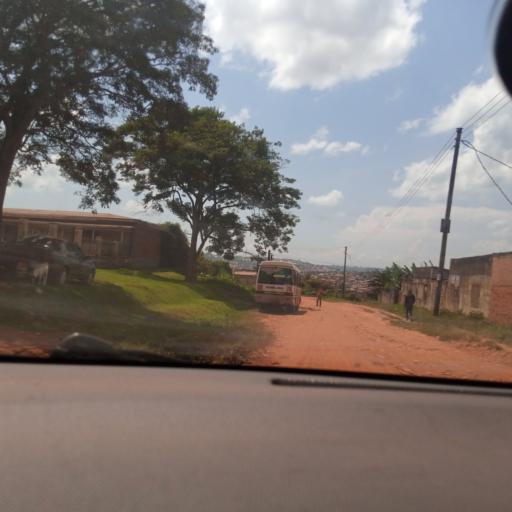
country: UG
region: Central Region
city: Masaka
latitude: -0.3312
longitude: 31.7440
